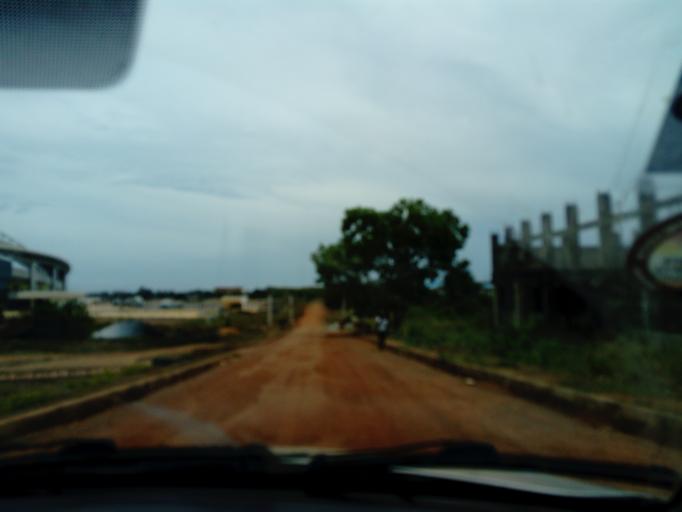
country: GH
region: Central
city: Cape Coast
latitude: 5.1369
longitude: -1.2847
